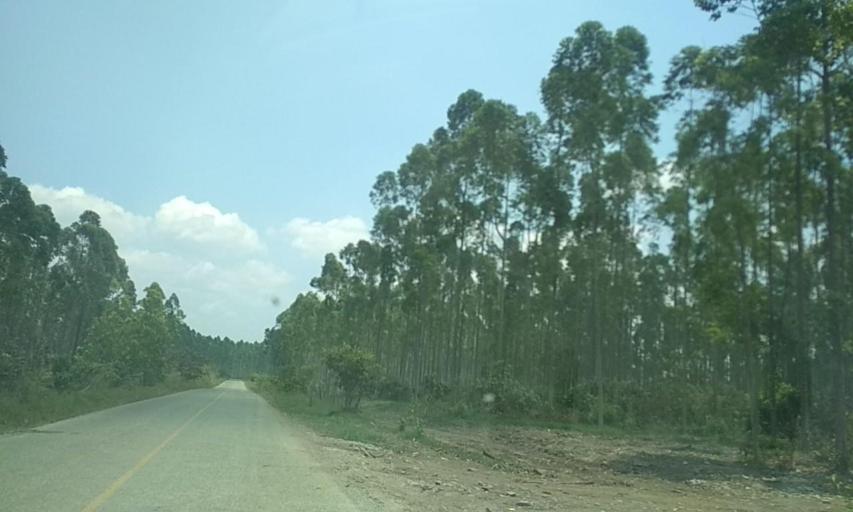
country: MX
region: Tabasco
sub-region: Huimanguillo
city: Francisco Rueda
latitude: 17.8409
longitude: -93.8866
